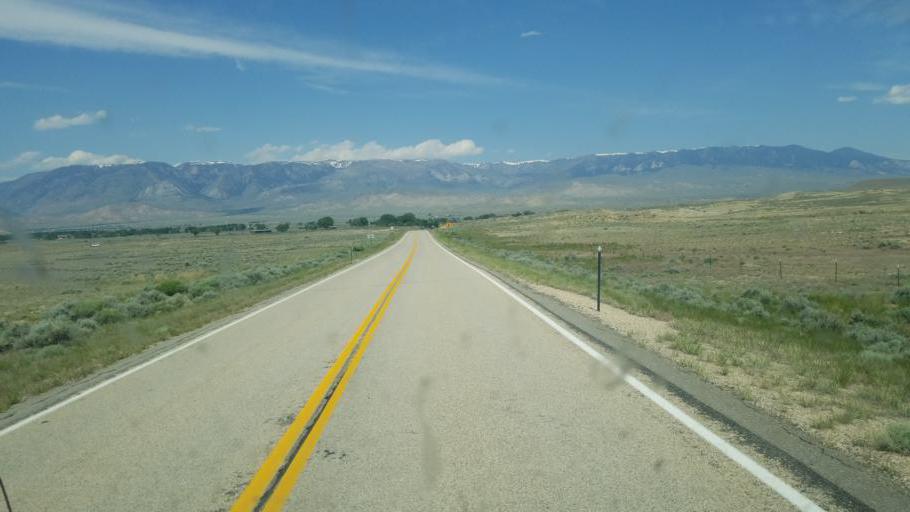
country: US
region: Montana
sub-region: Carbon County
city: Red Lodge
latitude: 44.9001
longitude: -109.0992
